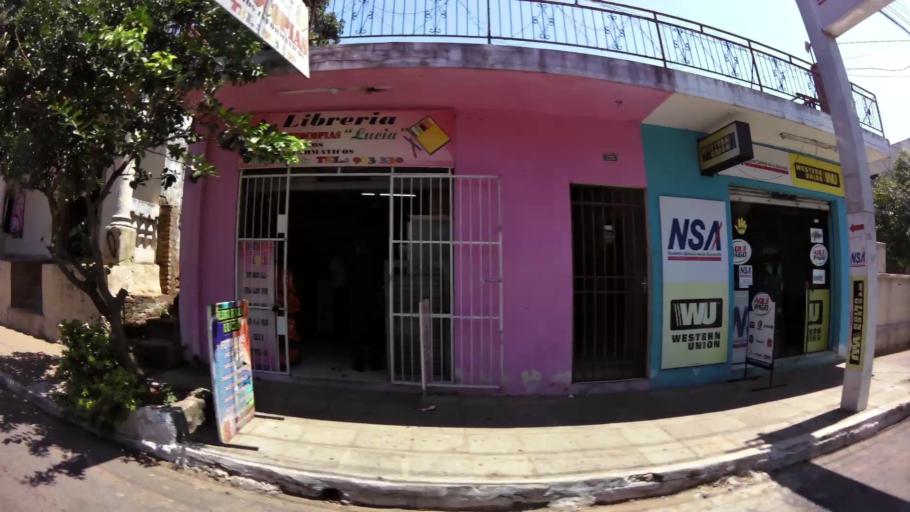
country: PY
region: Central
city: Nemby
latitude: -25.3944
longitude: -57.5458
